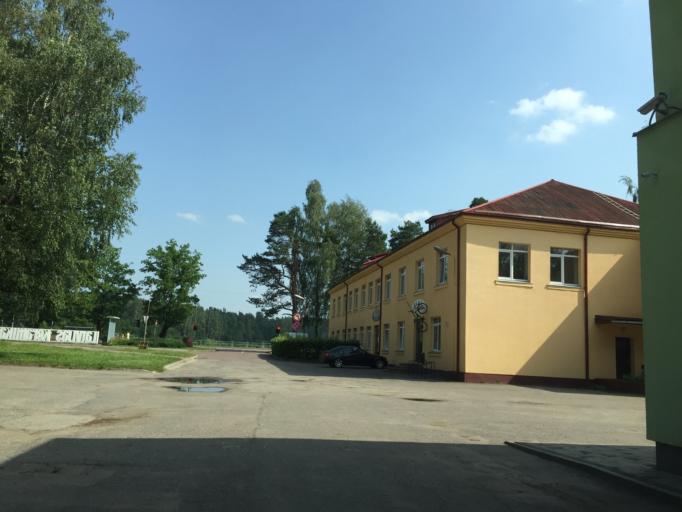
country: LV
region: Ozolnieku
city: Ozolnieki
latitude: 56.6727
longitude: 23.7644
